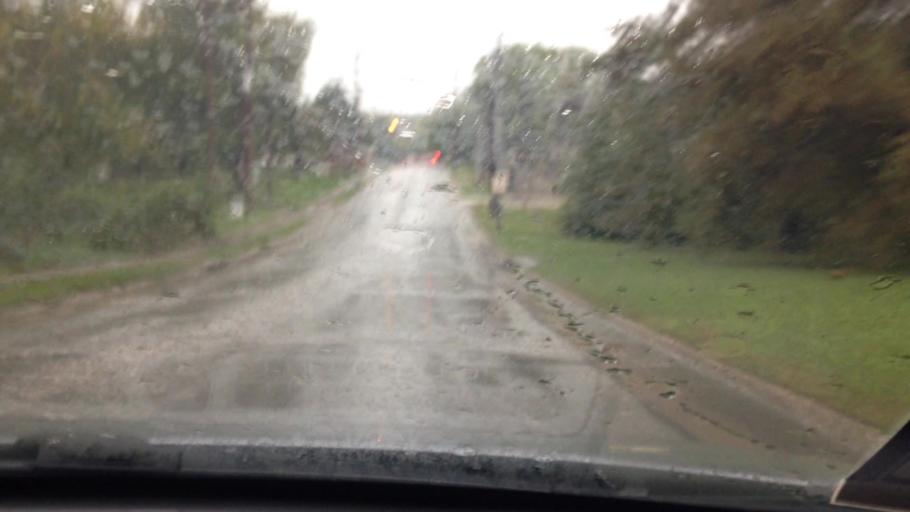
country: US
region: Kansas
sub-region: Leavenworth County
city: Leavenworth
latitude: 39.2959
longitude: -94.9238
